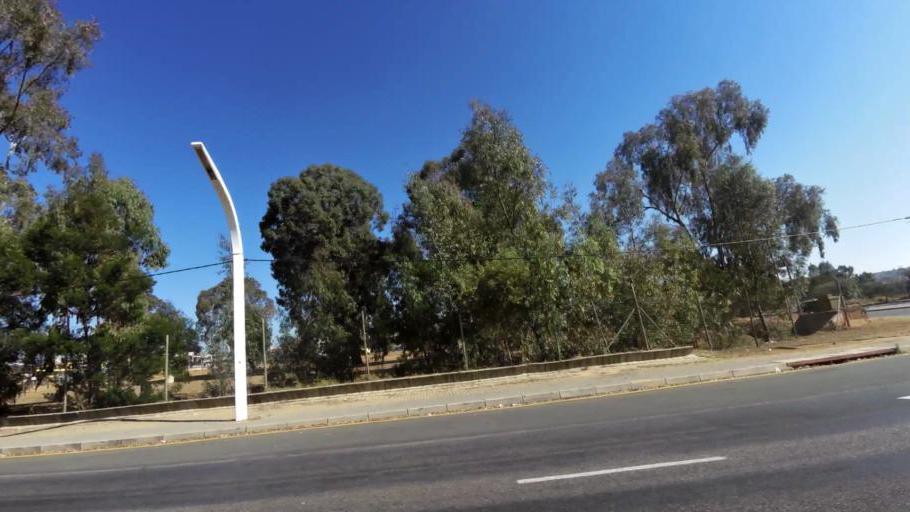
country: ZA
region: Gauteng
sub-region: City of Johannesburg Metropolitan Municipality
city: Johannesburg
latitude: -26.2397
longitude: 27.9855
